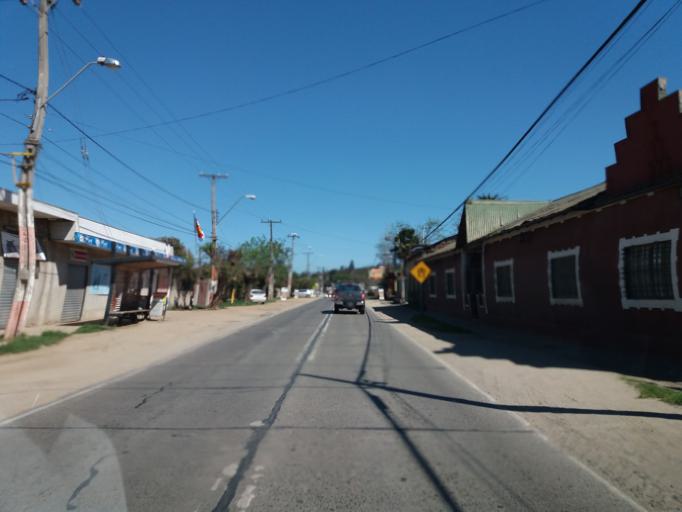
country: CL
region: Valparaiso
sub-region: Provincia de Marga Marga
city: Limache
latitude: -32.9958
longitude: -71.2302
